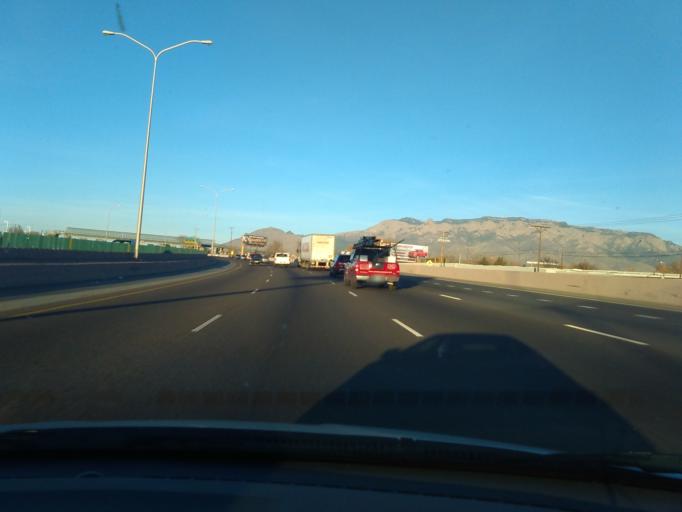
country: US
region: New Mexico
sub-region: Bernalillo County
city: North Valley
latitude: 35.1436
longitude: -106.5922
